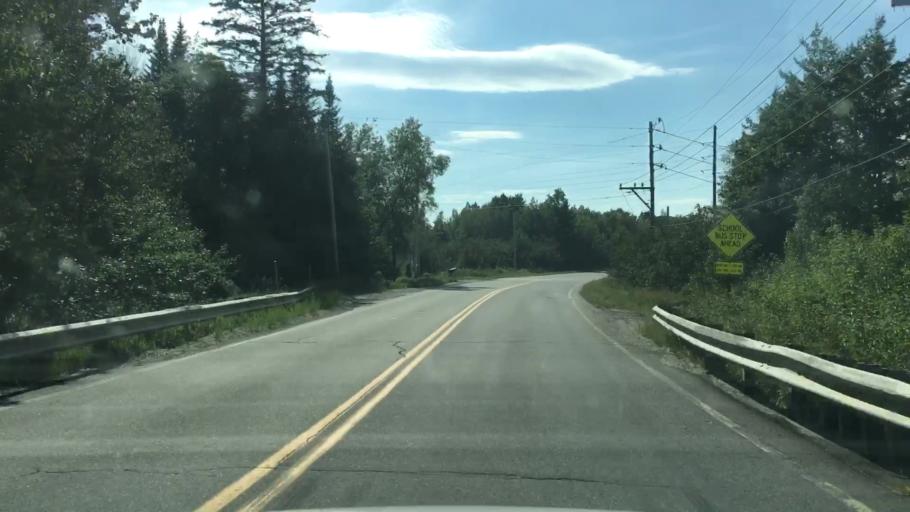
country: US
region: Maine
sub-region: Penobscot County
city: Lincoln
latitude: 45.3933
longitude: -68.5186
